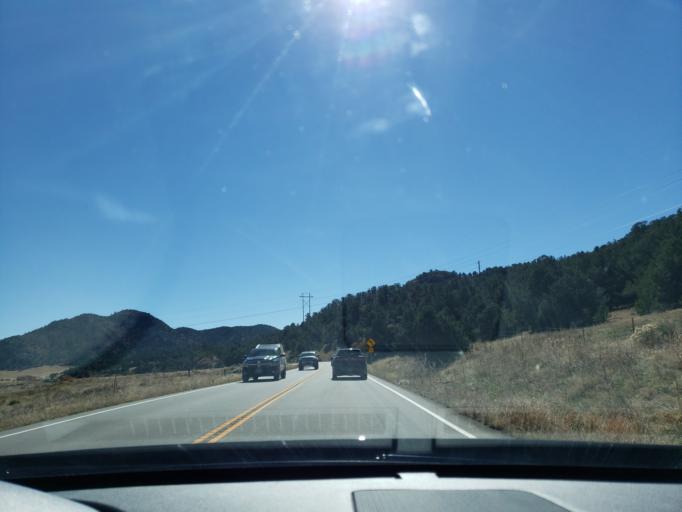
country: US
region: Colorado
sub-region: Fremont County
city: Canon City
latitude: 38.5920
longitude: -105.4245
